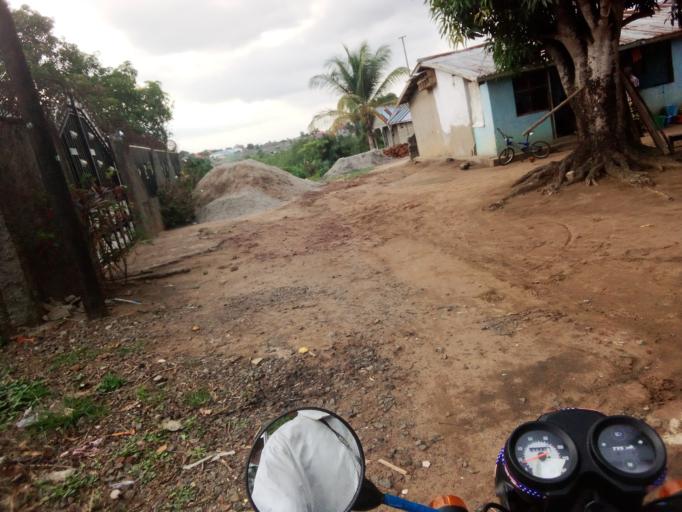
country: SL
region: Western Area
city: Waterloo
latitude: 8.3448
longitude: -13.0698
